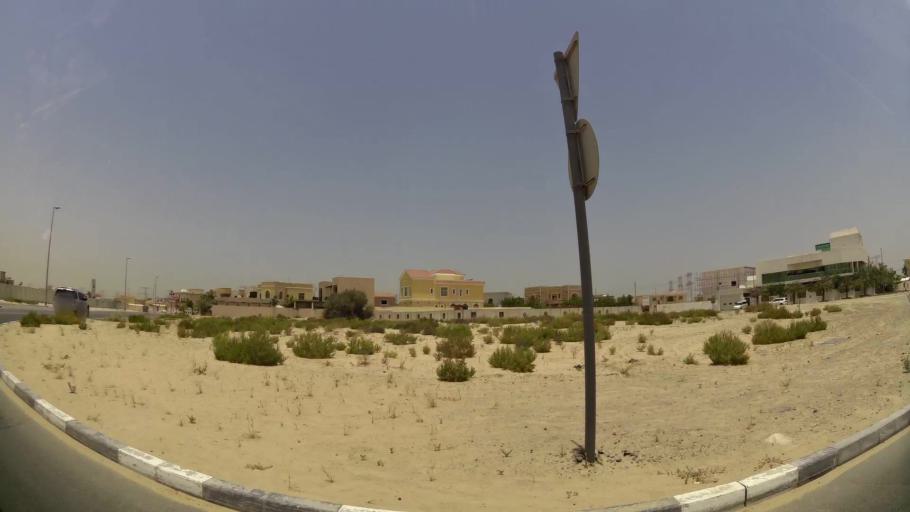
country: AE
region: Dubai
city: Dubai
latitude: 25.0916
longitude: 55.2301
